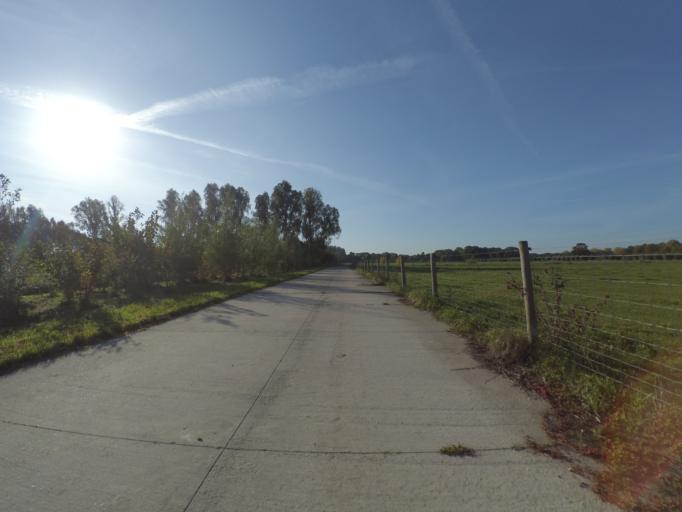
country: NL
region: Utrecht
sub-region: Gemeente Bunnik
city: Bunnik
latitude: 52.0817
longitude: 5.1899
